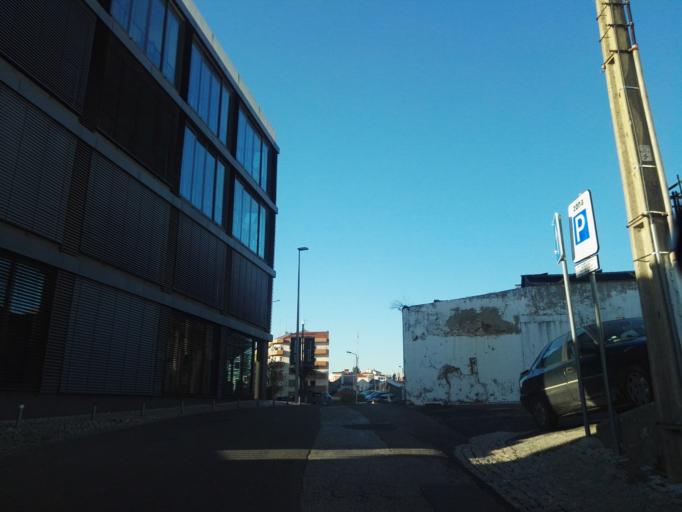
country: PT
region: Santarem
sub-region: Santarem
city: Santarem
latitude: 39.2324
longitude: -8.6830
